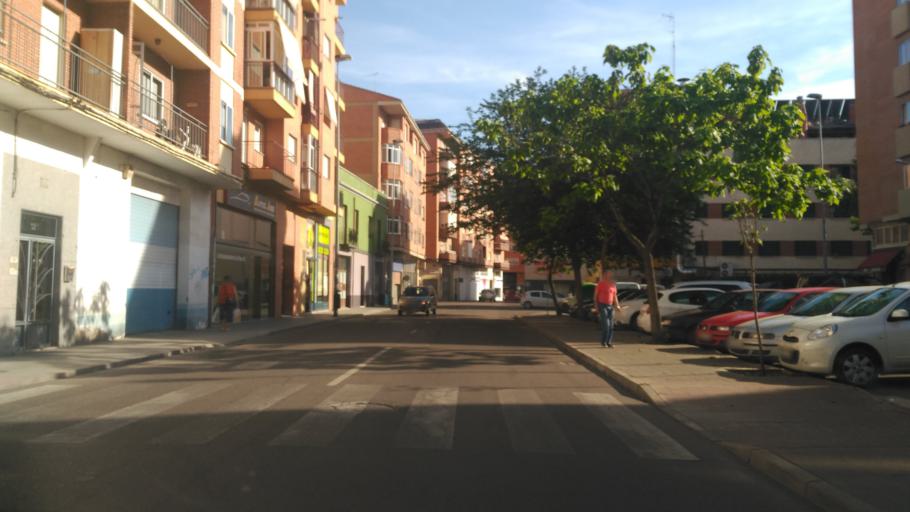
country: ES
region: Castille and Leon
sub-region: Provincia de Zamora
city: Zamora
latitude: 41.5079
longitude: -5.7482
